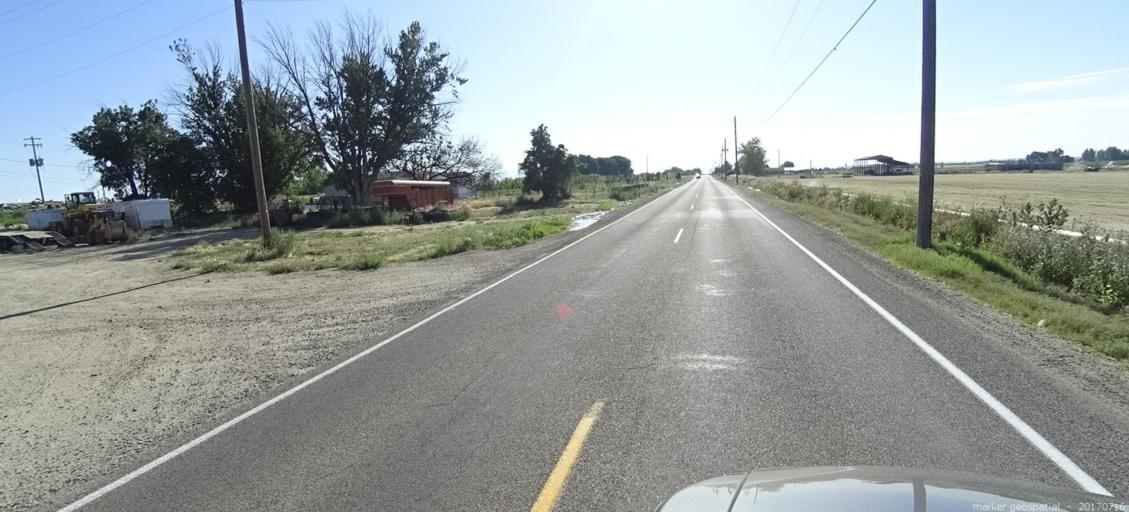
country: US
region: Idaho
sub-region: Ada County
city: Meridian
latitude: 43.5464
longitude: -116.3685
